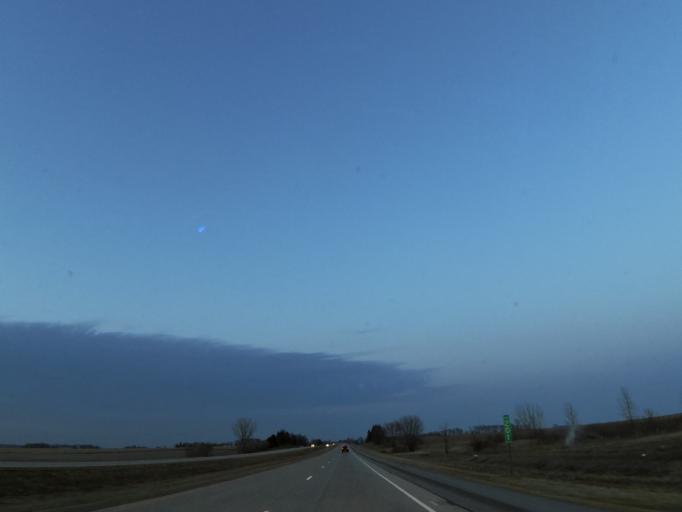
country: US
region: Minnesota
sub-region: Mower County
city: Grand Meadow
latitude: 43.7941
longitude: -92.6023
